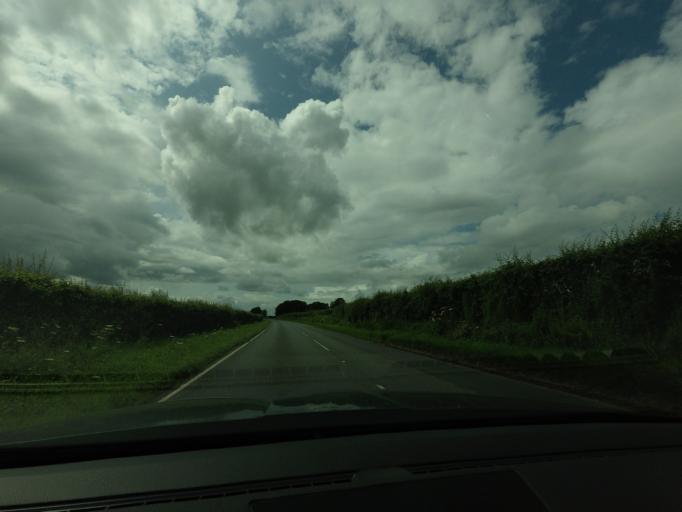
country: GB
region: Scotland
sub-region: Aberdeenshire
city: Whitehills
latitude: 57.6558
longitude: -2.6090
